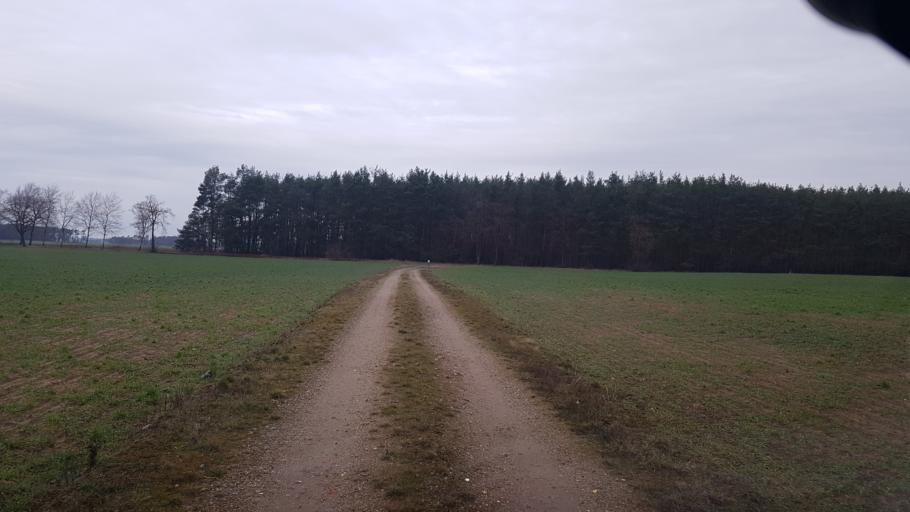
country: DE
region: Brandenburg
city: Bad Liebenwerda
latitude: 51.5368
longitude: 13.3330
